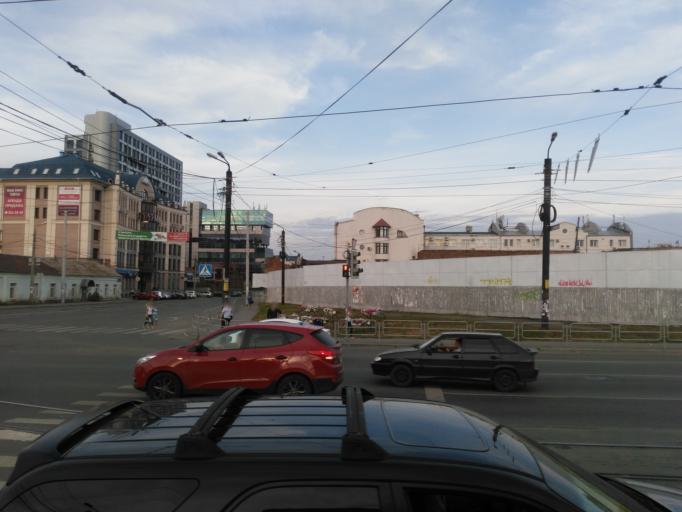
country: RU
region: Chelyabinsk
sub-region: Gorod Chelyabinsk
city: Chelyabinsk
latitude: 55.1678
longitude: 61.4037
